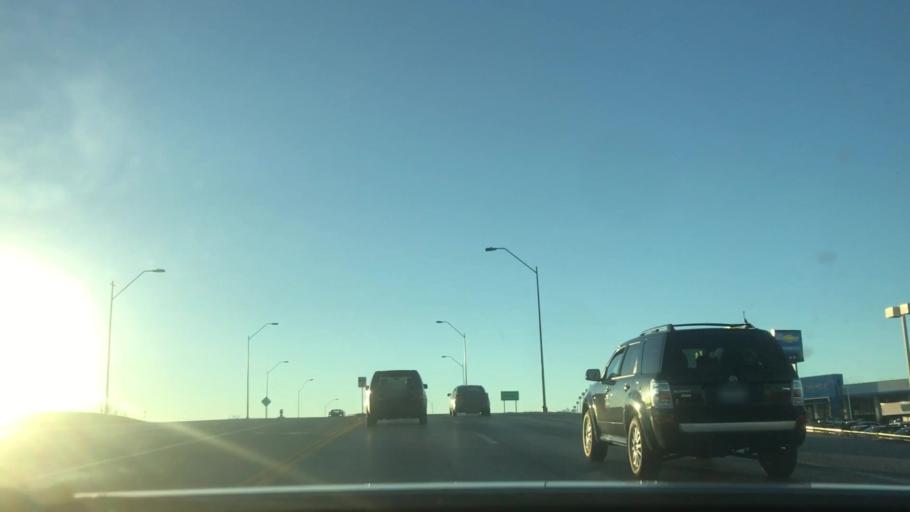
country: US
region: Missouri
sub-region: Platte County
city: Riverside
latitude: 39.1810
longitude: -94.5822
